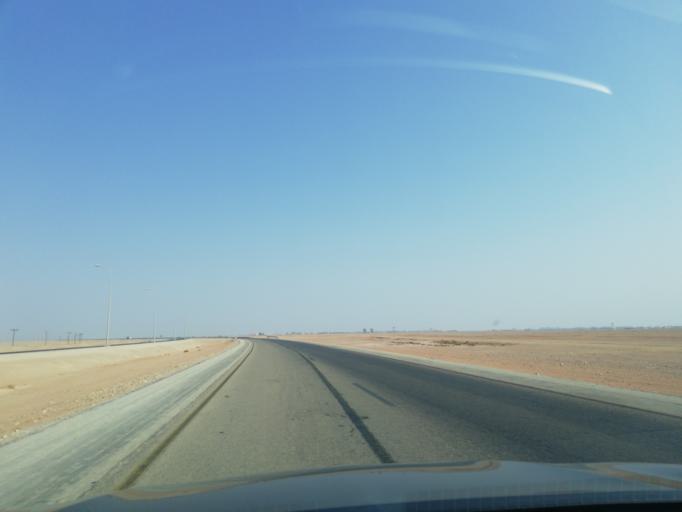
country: OM
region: Zufar
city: Salalah
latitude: 17.7156
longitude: 54.0251
